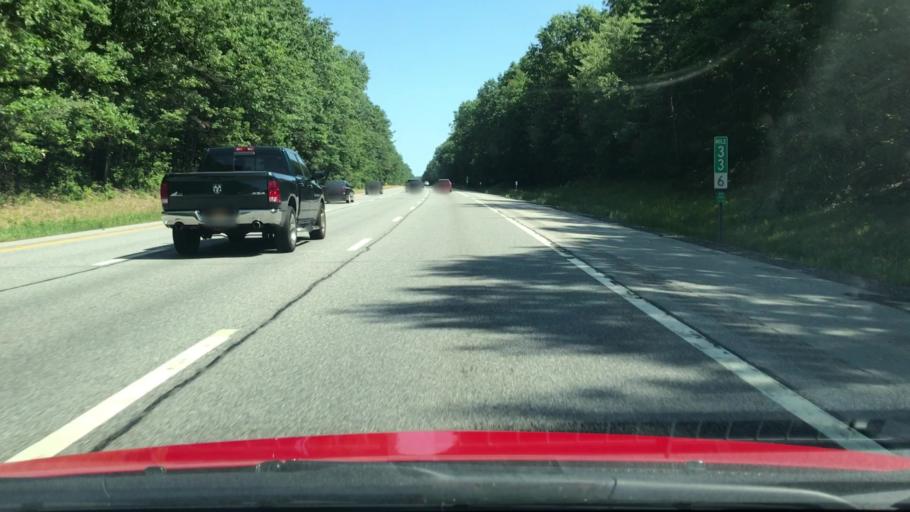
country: US
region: New York
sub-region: Saratoga County
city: Saratoga Springs
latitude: 43.1371
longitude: -73.7306
